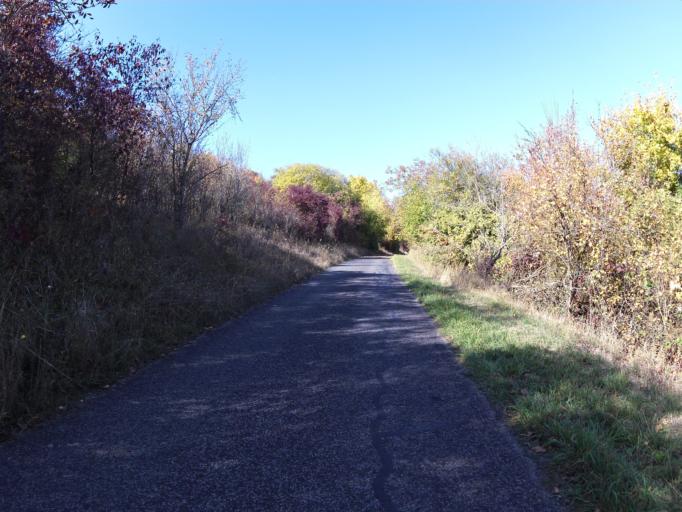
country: DE
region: Bavaria
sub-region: Regierungsbezirk Unterfranken
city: Eibelstadt
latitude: 49.7170
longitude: 9.9933
